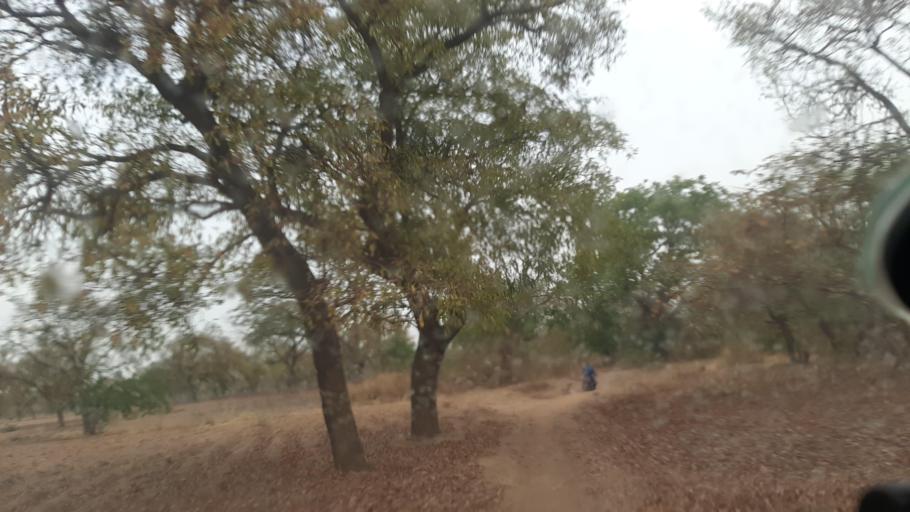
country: BF
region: Boucle du Mouhoun
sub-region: Province des Banwa
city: Salanso
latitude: 11.8587
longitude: -4.4331
